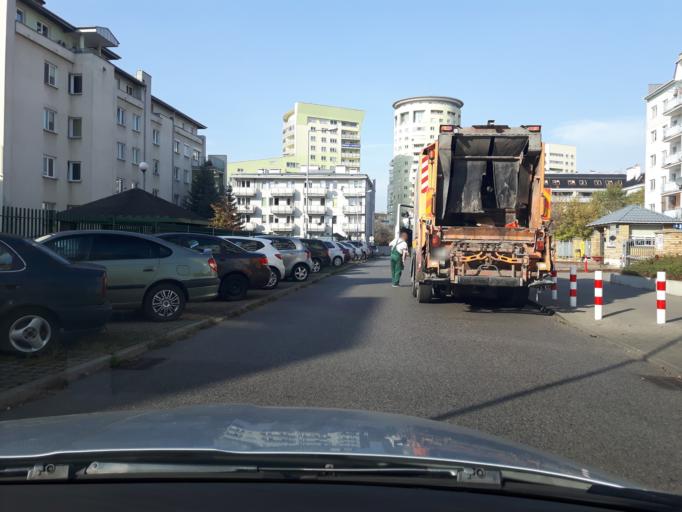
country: PL
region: Masovian Voivodeship
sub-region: Warszawa
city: Praga Poludnie
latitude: 52.2312
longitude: 21.0845
